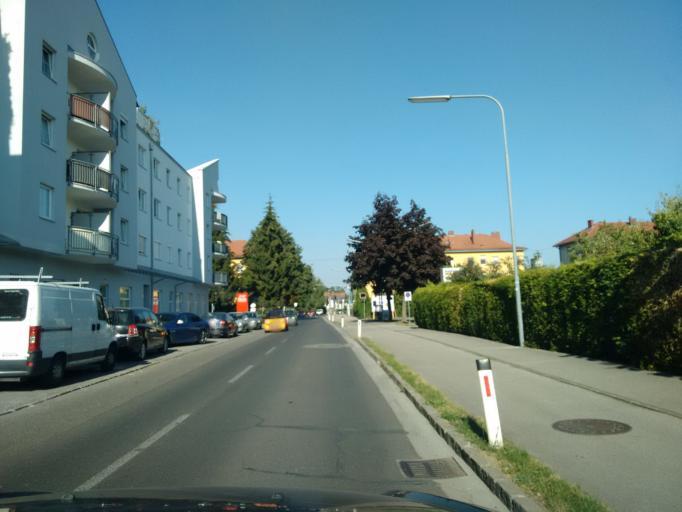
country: AT
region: Upper Austria
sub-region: Politischer Bezirk Linz-Land
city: Traun
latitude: 48.2232
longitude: 14.2423
